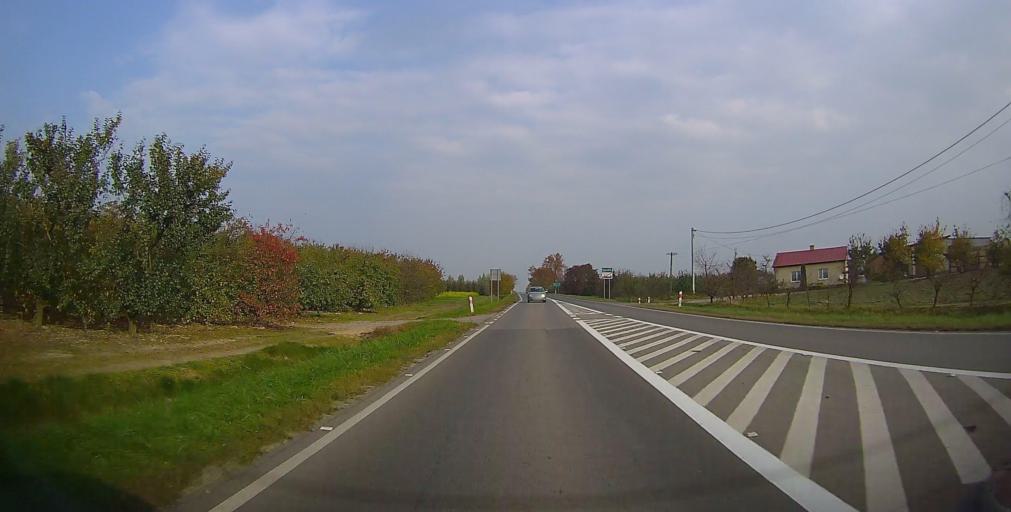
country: PL
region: Masovian Voivodeship
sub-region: Powiat grojecki
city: Mogielnica
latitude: 51.7511
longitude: 20.7642
